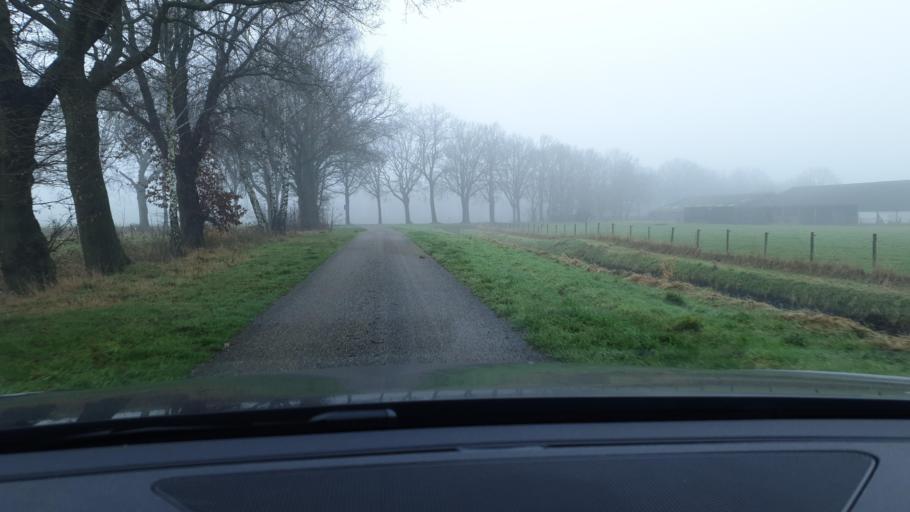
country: NL
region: North Brabant
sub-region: Gemeente Asten
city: Asten
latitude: 51.3661
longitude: 5.8432
